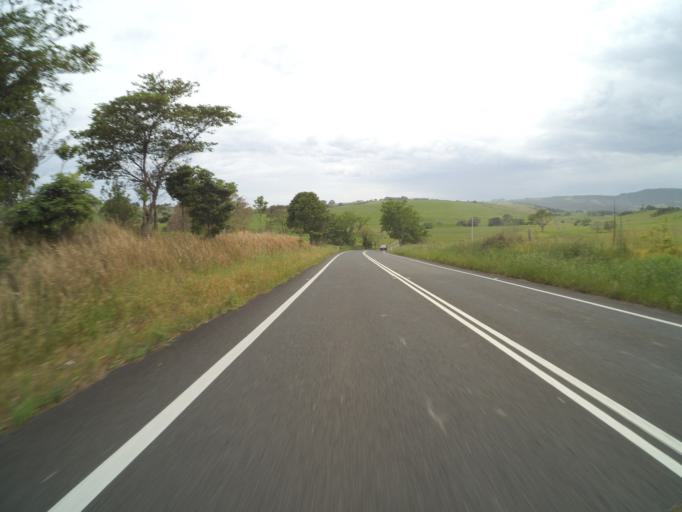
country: AU
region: New South Wales
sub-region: Kiama
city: Kiama
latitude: -34.6565
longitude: 150.8175
